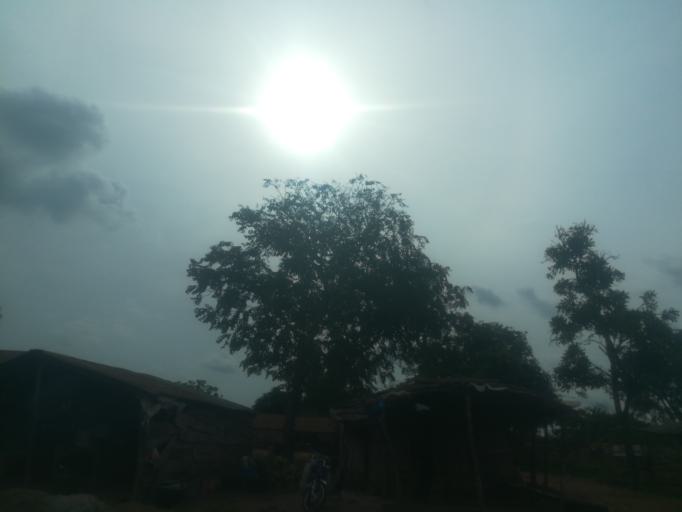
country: NG
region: Ogun
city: Ayetoro
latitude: 7.3143
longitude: 3.0707
